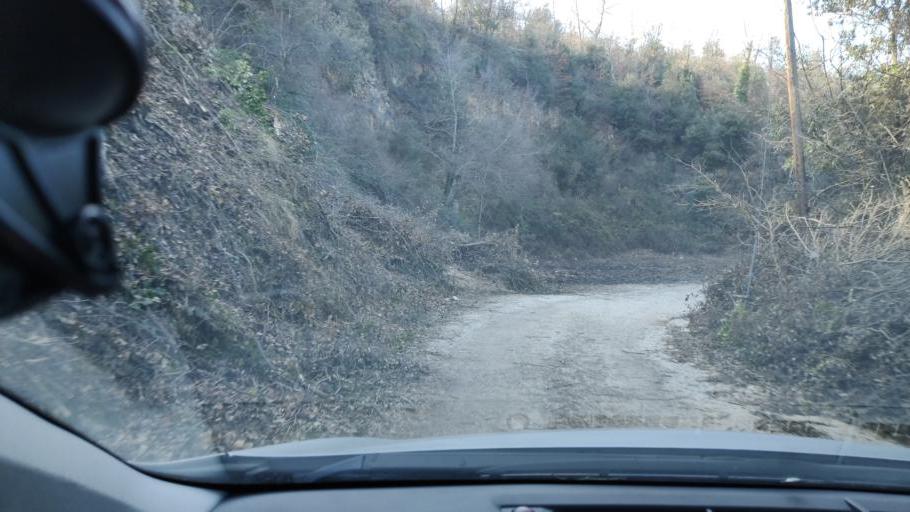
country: IT
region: Umbria
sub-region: Provincia di Terni
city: Amelia
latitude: 42.5638
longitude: 12.4398
